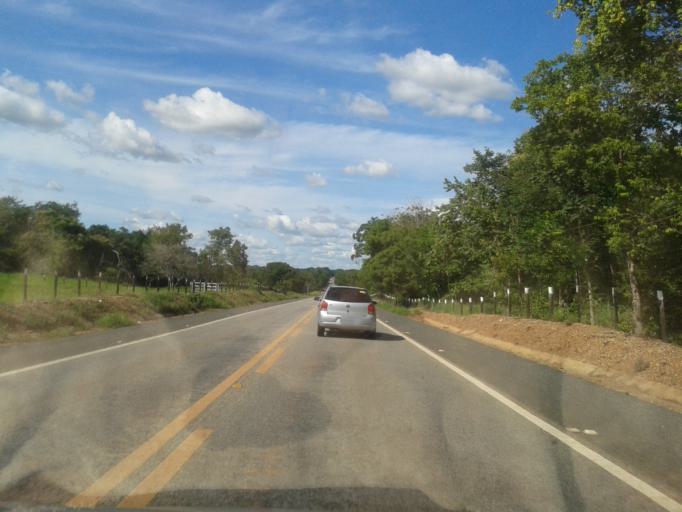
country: BR
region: Goias
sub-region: Mozarlandia
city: Mozarlandia
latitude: -15.0041
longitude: -50.5905
